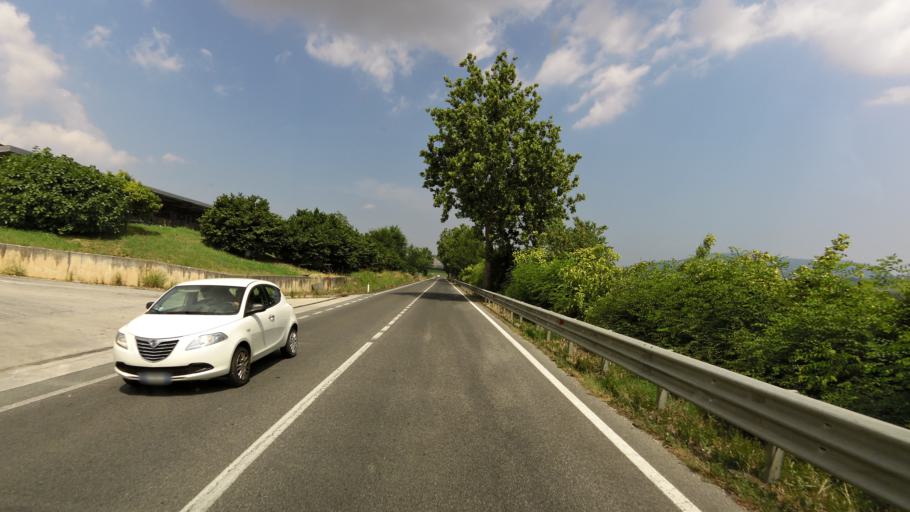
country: IT
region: The Marches
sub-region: Provincia di Ancona
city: Castelfidardo
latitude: 43.4783
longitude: 13.5800
